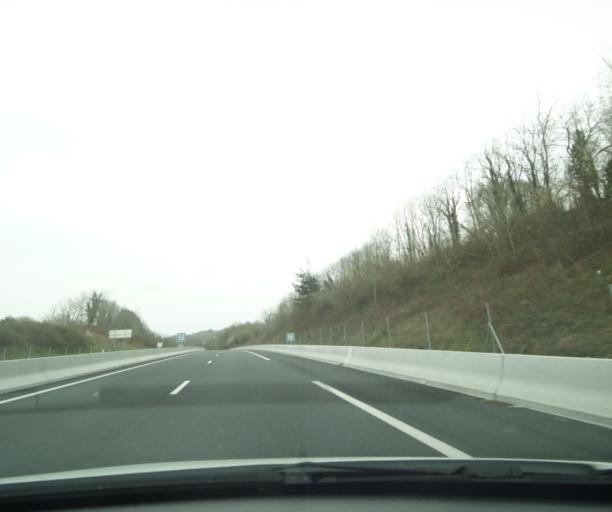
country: FR
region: Aquitaine
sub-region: Departement des Pyrenees-Atlantiques
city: Briscous
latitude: 43.4464
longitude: -1.3690
